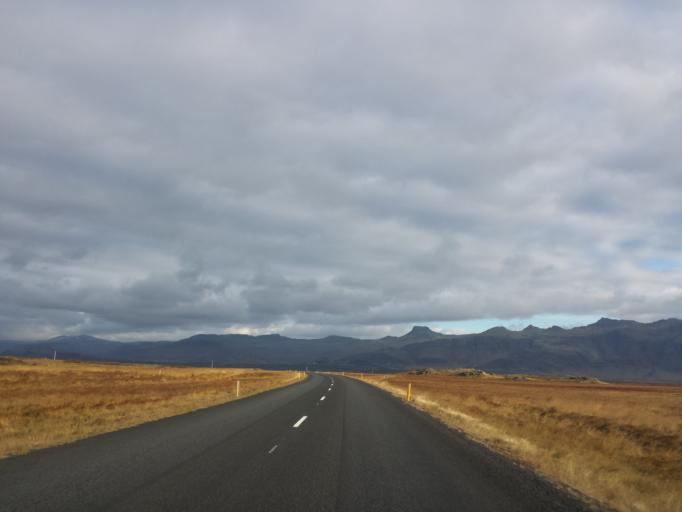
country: IS
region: West
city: Stykkisholmur
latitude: 64.8464
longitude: -22.3533
